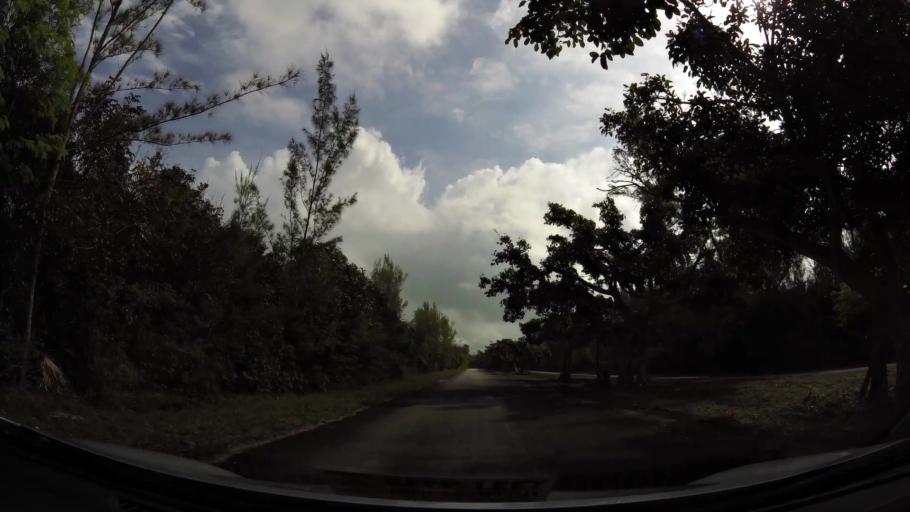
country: BS
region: Freeport
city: Lucaya
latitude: 26.5522
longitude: -78.5501
